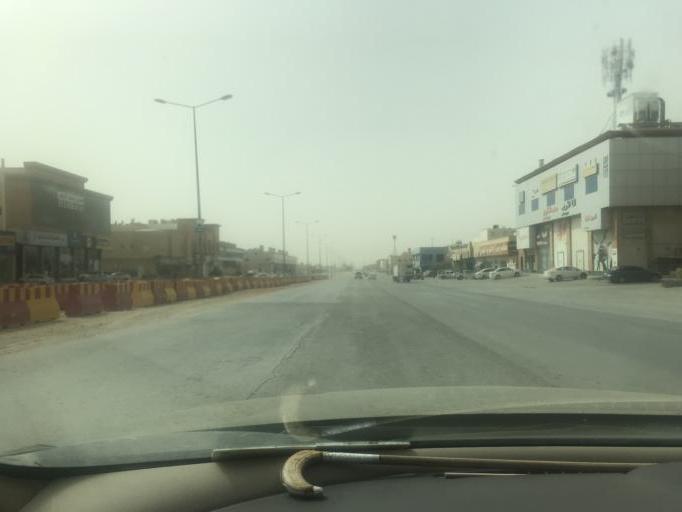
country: SA
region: Ar Riyad
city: Riyadh
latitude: 24.8083
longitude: 46.6015
